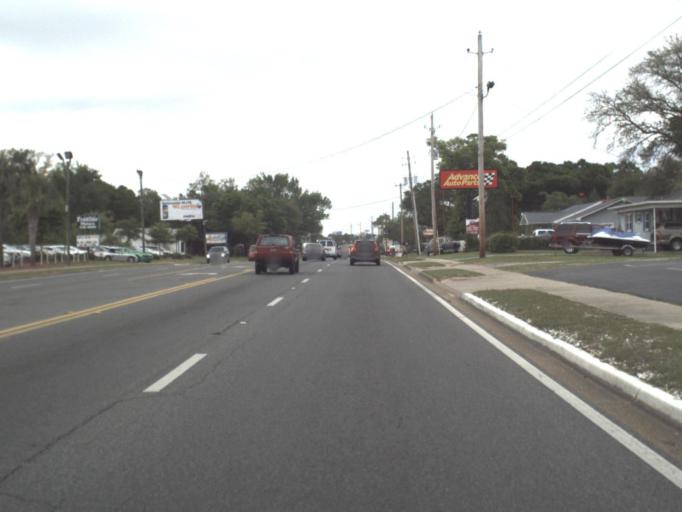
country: US
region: Florida
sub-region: Escambia County
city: Brent
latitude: 30.4651
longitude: -87.2477
